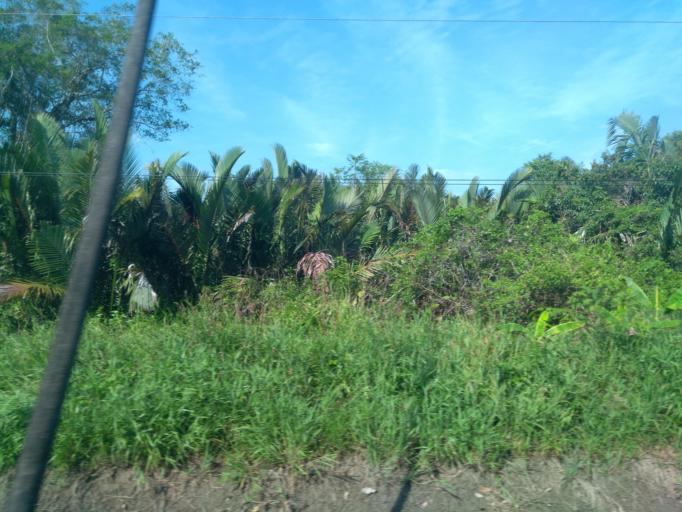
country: MY
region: Sarawak
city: Kuching
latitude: 1.6571
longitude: 110.4397
